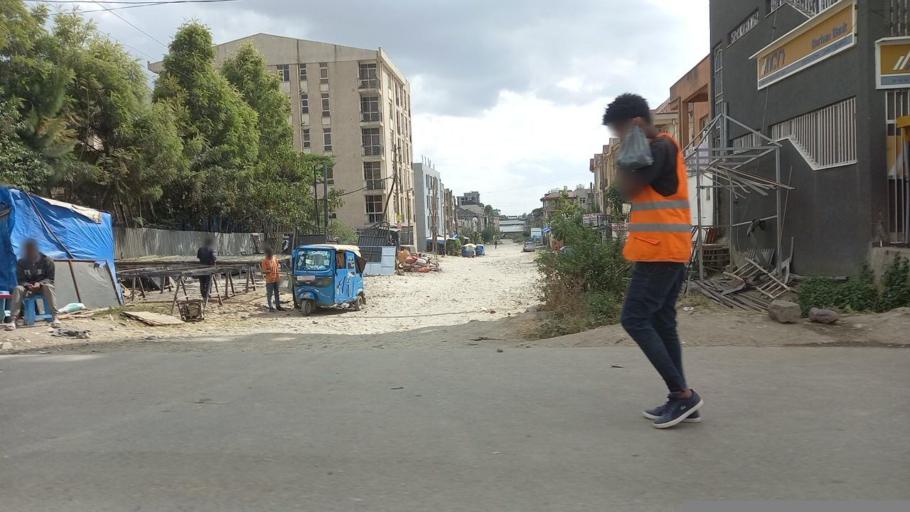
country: ET
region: Adis Abeba
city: Addis Ababa
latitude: 9.0097
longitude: 38.8563
